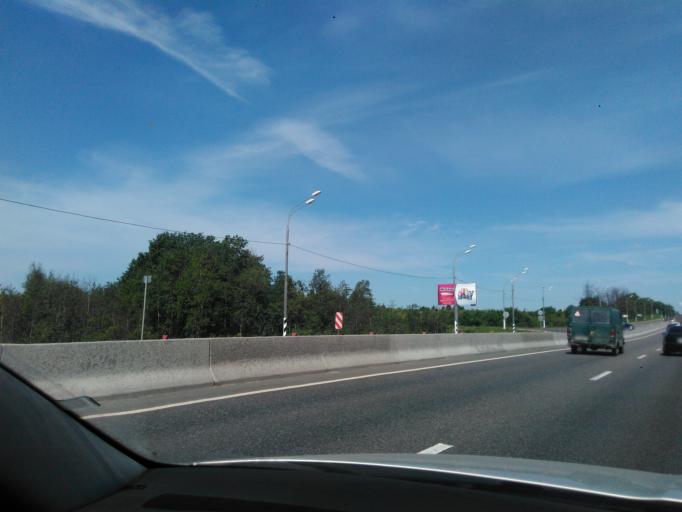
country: RU
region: Moskovskaya
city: Lozhki
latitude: 56.1081
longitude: 37.0931
